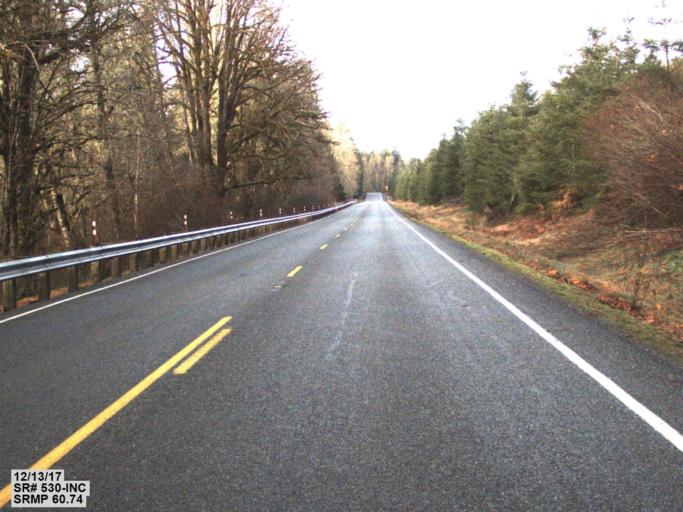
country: US
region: Washington
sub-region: Snohomish County
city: Darrington
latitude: 48.3986
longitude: -121.5519
